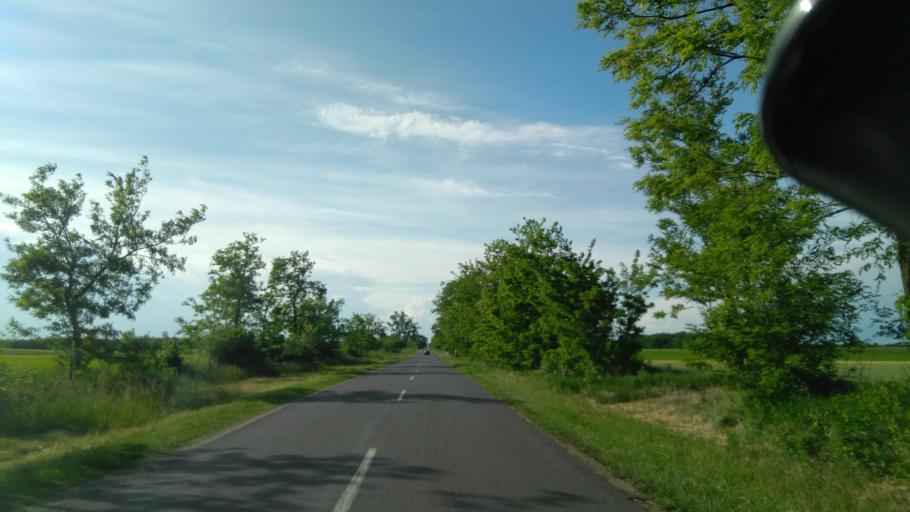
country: HU
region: Bekes
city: Lokoshaza
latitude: 46.4524
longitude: 21.2165
